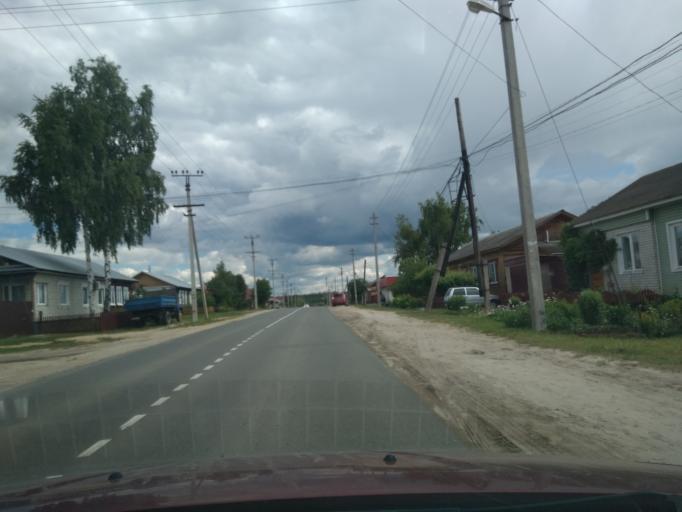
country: RU
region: Vladimir
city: Melenki
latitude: 55.3384
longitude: 41.6481
